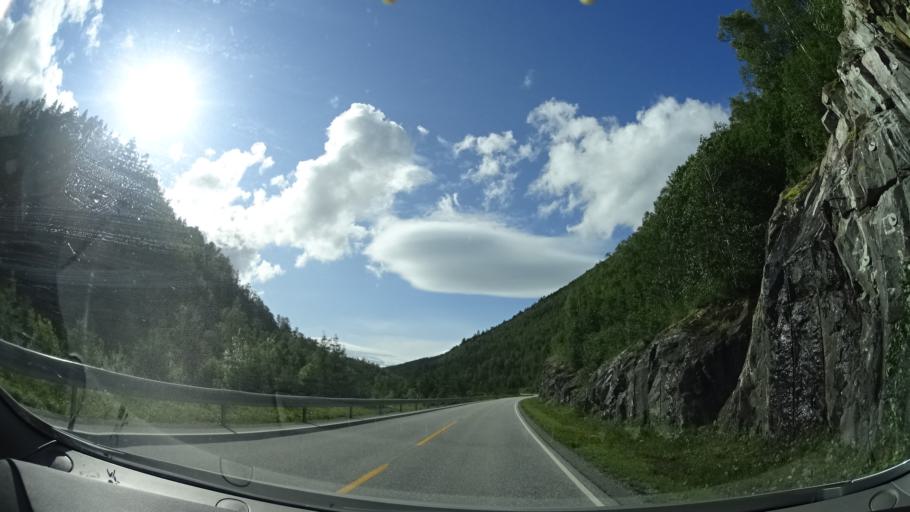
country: NO
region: Sor-Trondelag
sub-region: Hemne
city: Kyrksaeterora
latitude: 63.2112
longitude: 9.1464
